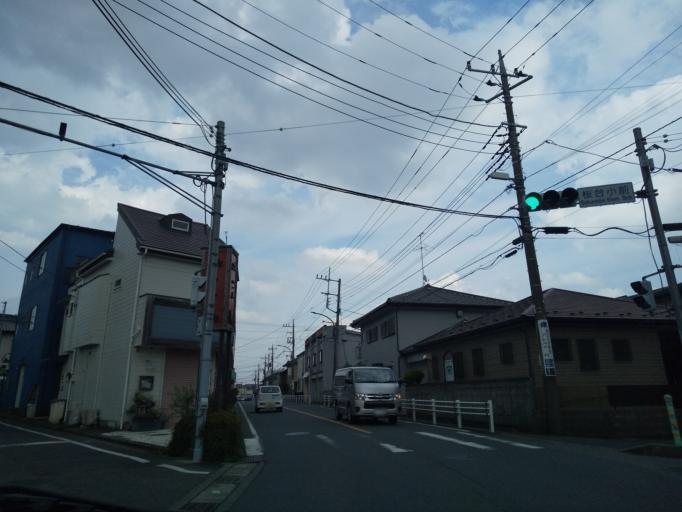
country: JP
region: Kanagawa
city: Zama
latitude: 35.5242
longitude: 139.4080
